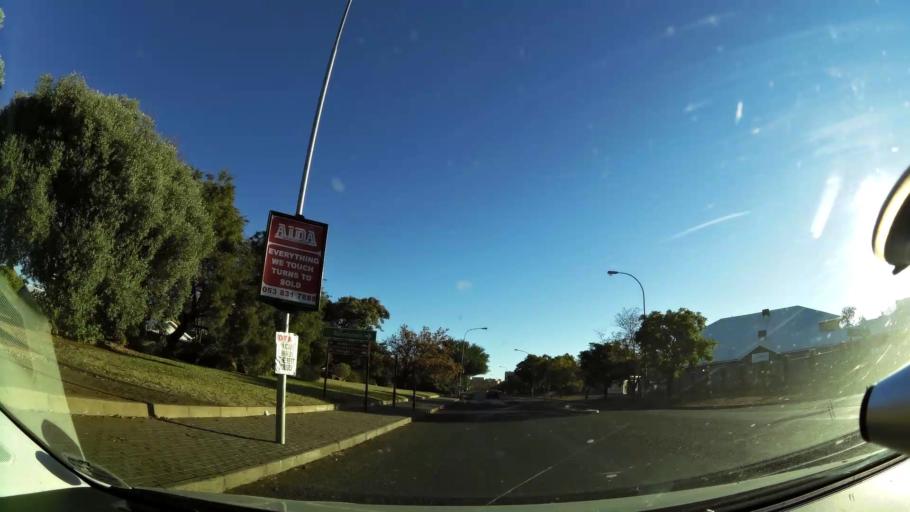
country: ZA
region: Northern Cape
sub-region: Frances Baard District Municipality
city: Kimberley
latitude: -28.7546
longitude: 24.7653
